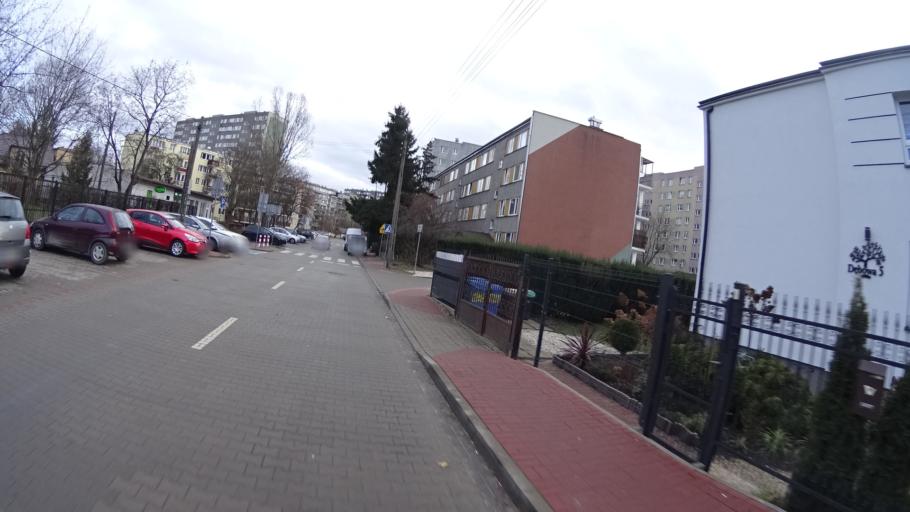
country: PL
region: Masovian Voivodeship
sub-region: Powiat pruszkowski
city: Pruszkow
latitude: 52.1581
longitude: 20.7858
